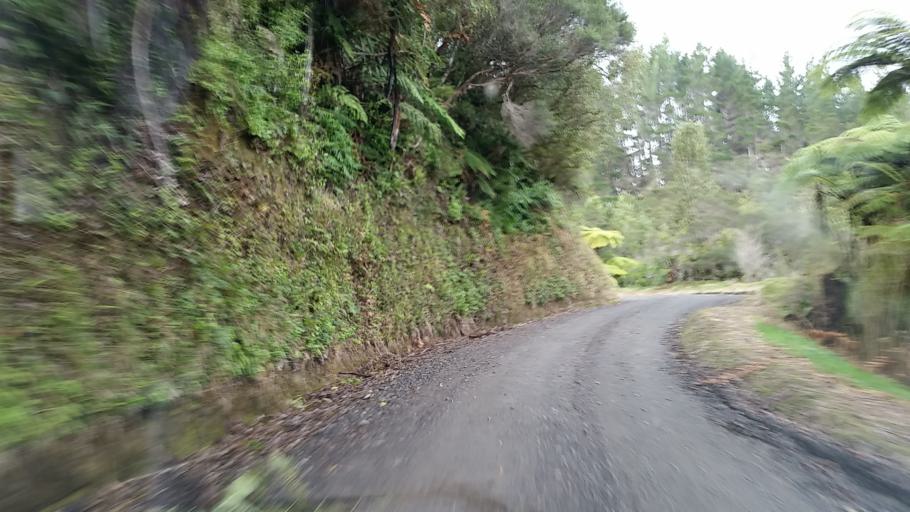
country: NZ
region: Taranaki
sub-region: New Plymouth District
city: Waitara
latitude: -39.1618
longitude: 174.5503
